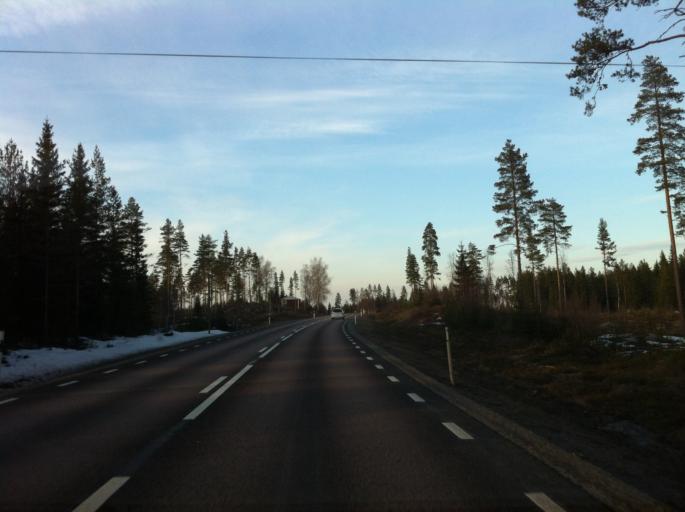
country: SE
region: Vaermland
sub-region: Filipstads Kommun
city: Lesjofors
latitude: 60.0498
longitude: 14.1421
